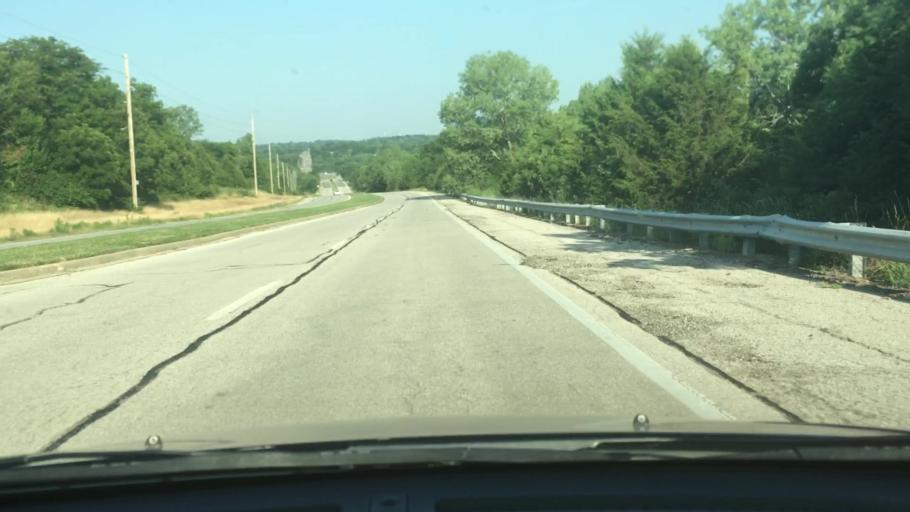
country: US
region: Missouri
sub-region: Jackson County
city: Grandview
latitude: 38.8850
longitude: -94.4796
